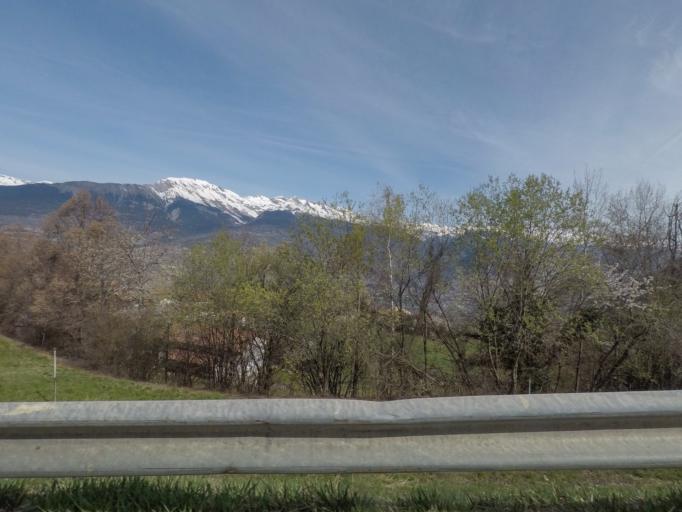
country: CH
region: Valais
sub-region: Herens District
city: Vex
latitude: 46.2200
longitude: 7.4012
